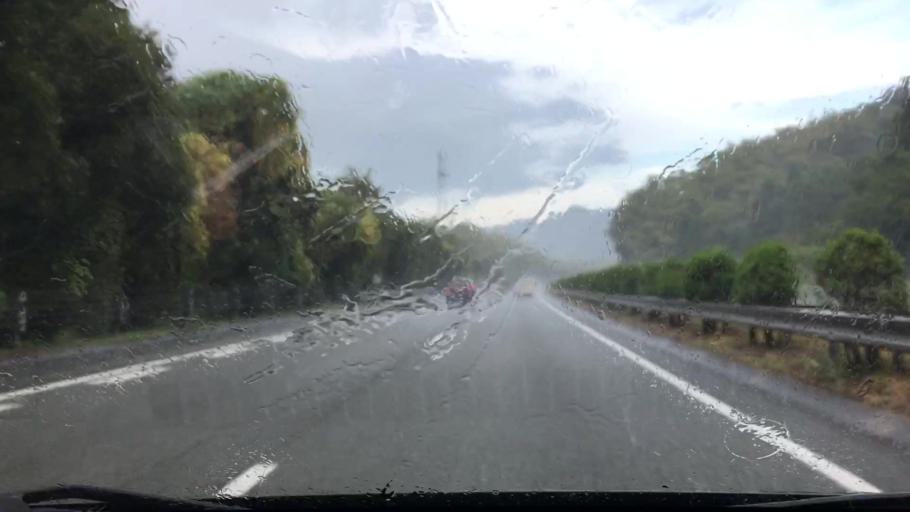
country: JP
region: Fukuoka
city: Kitakyushu
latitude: 33.8089
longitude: 130.8346
